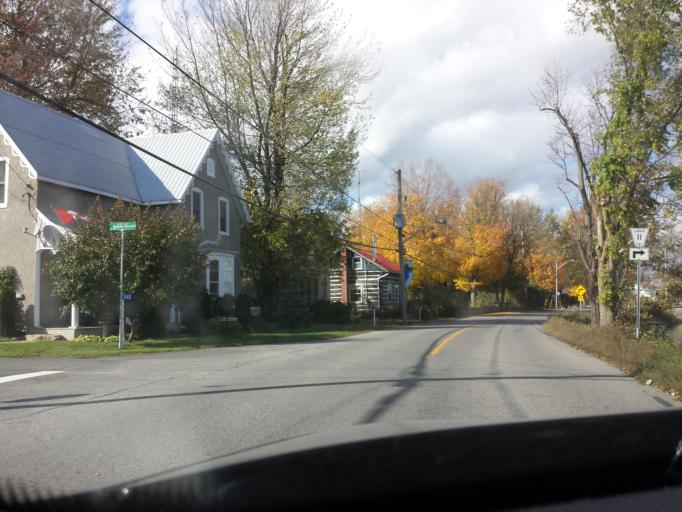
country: CA
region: Ontario
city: Carleton Place
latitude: 45.1804
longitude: -76.1255
